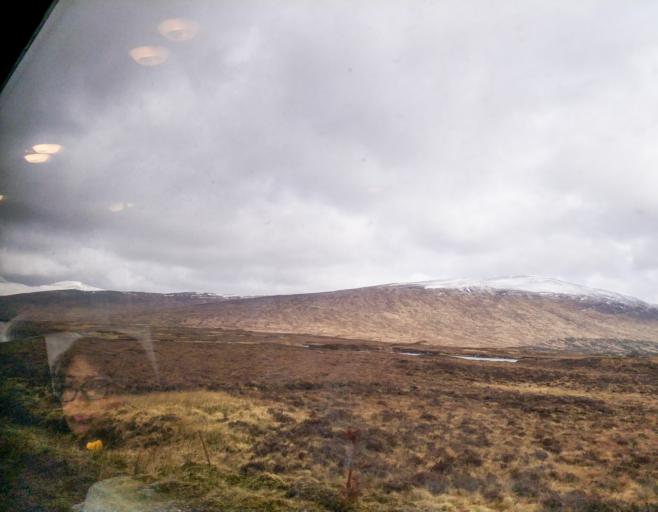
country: GB
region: Scotland
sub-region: Highland
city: Spean Bridge
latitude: 56.7518
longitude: -4.6782
